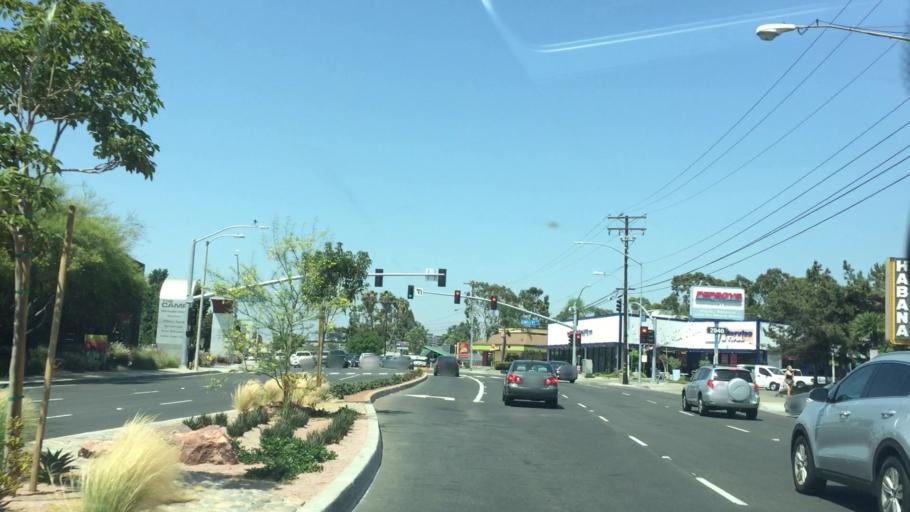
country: US
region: California
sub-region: Orange County
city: Costa Mesa
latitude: 33.6776
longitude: -117.8866
